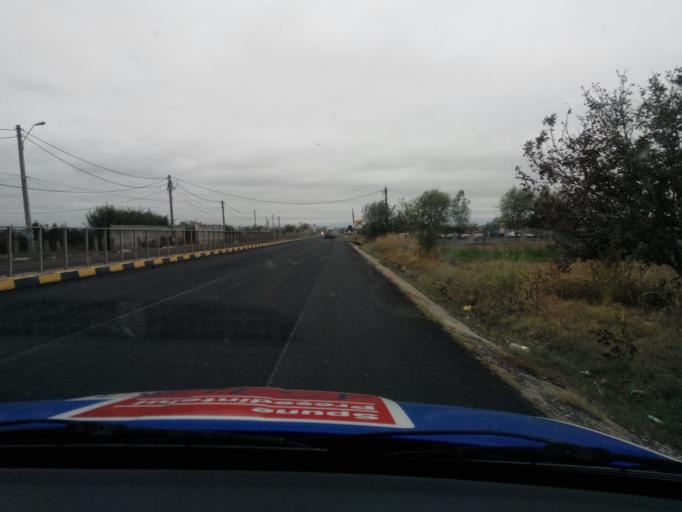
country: RO
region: Giurgiu
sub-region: Comuna Daia
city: Daia
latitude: 43.9800
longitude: 25.9883
